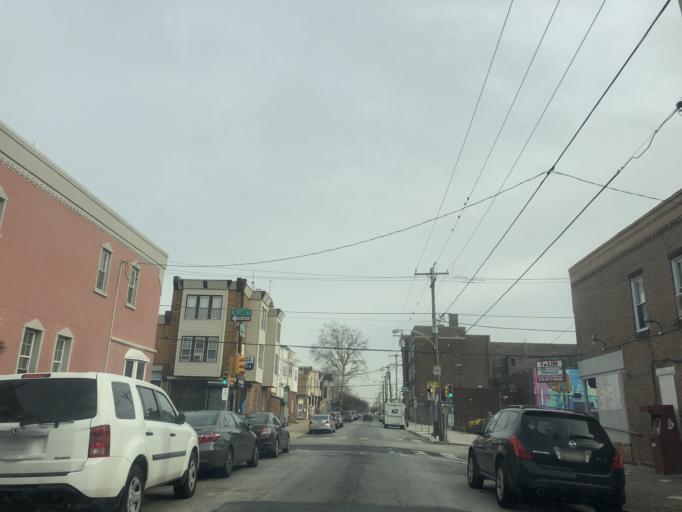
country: US
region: Pennsylvania
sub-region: Philadelphia County
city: Philadelphia
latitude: 39.9176
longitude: -75.1565
